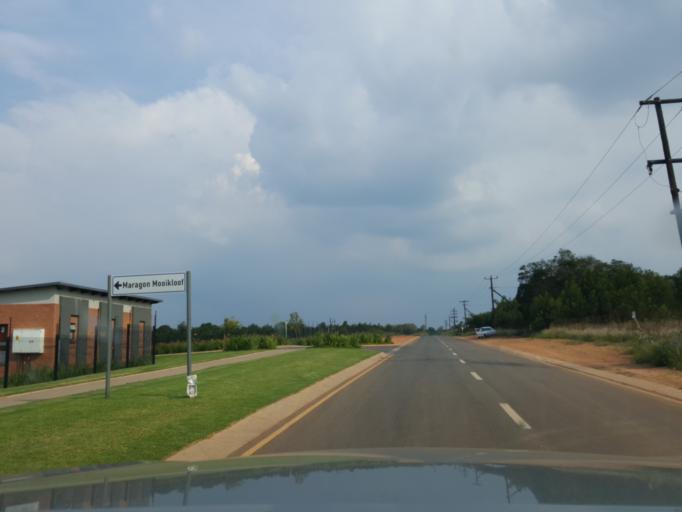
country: ZA
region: Gauteng
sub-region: City of Tshwane Metropolitan Municipality
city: Centurion
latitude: -25.8573
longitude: 28.3261
